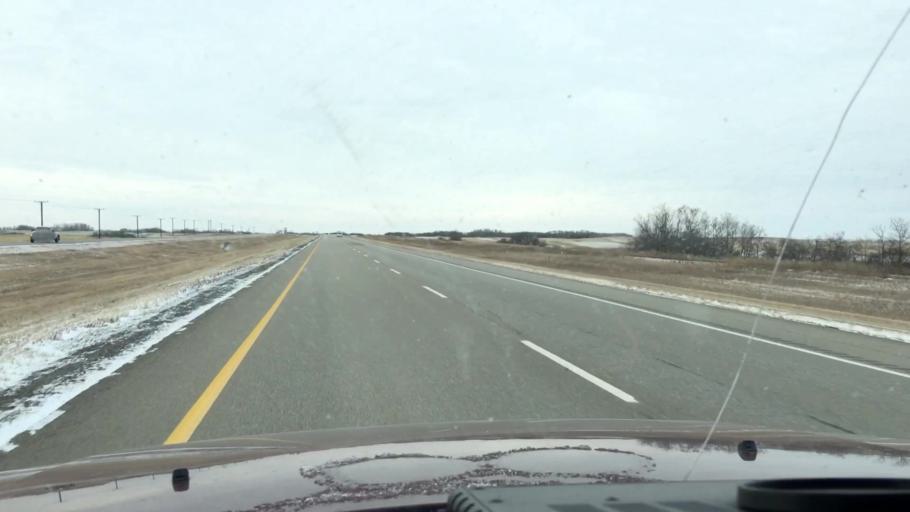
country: CA
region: Saskatchewan
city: Watrous
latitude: 51.3965
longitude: -106.1723
